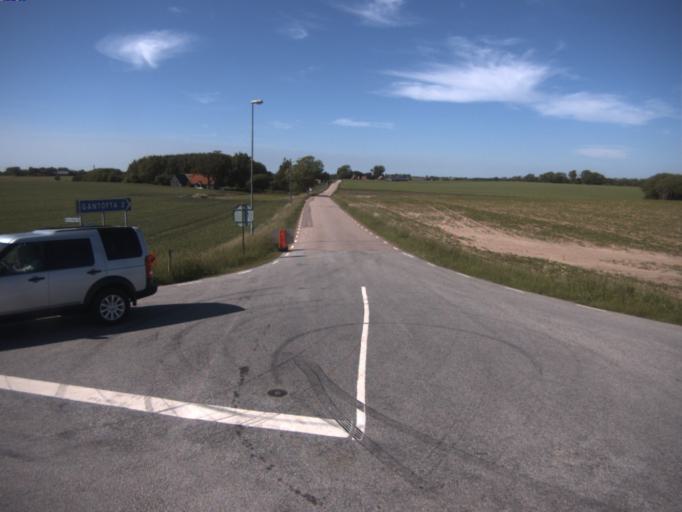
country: SE
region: Skane
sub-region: Helsingborg
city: Gantofta
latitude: 55.9750
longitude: 12.8129
